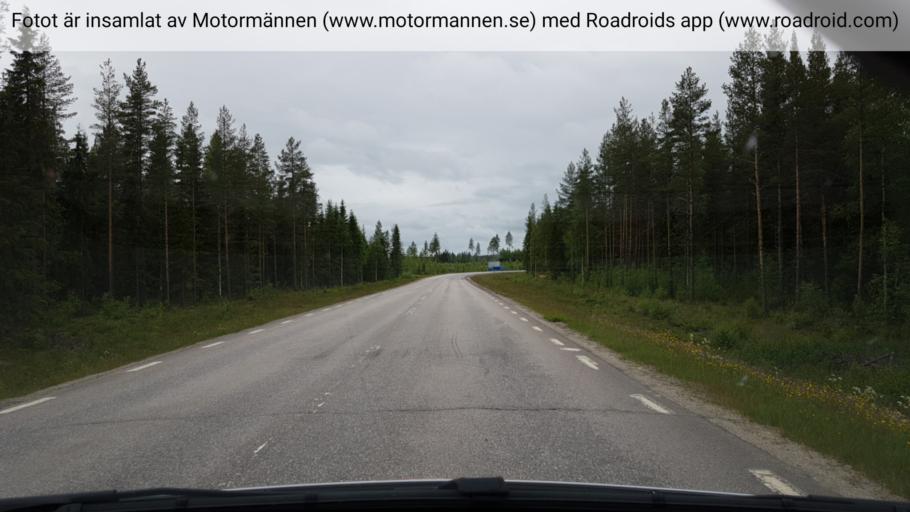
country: SE
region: Vaesterbotten
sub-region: Vindelns Kommun
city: Vindeln
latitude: 64.0546
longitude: 19.6571
